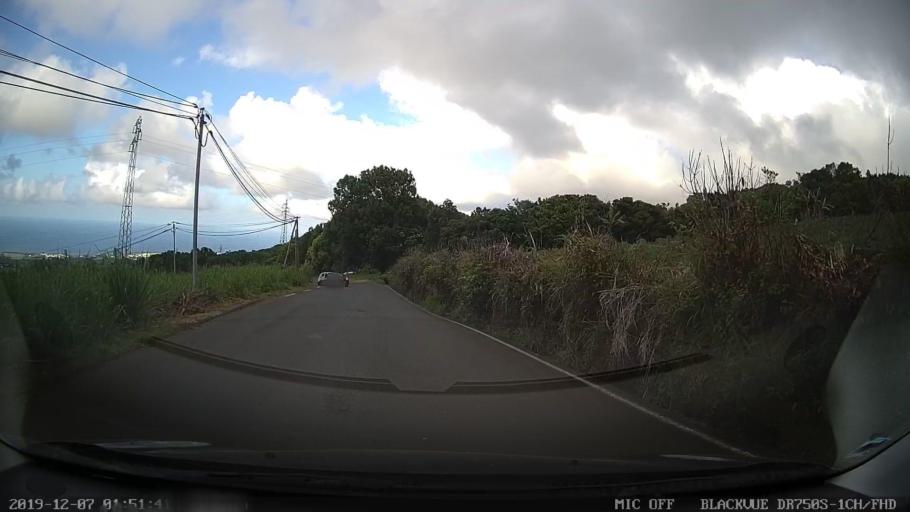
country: RE
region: Reunion
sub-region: Reunion
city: Sainte-Marie
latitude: -20.9420
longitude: 55.5346
